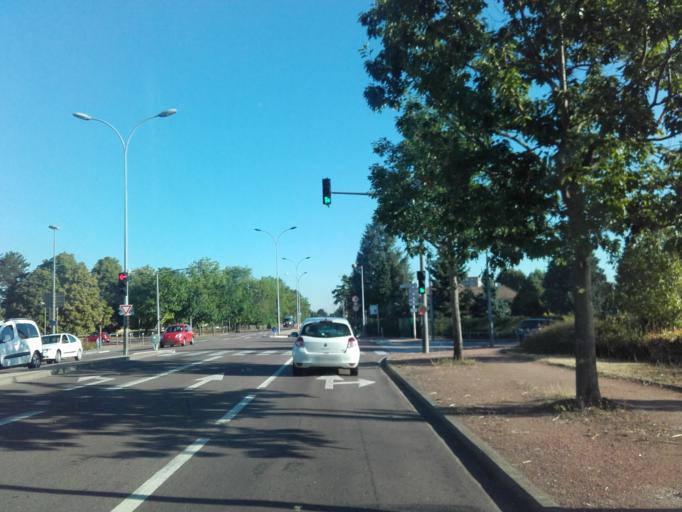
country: FR
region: Bourgogne
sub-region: Departement de Saone-et-Loire
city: Champforgeuil
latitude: 46.8094
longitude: 4.8434
